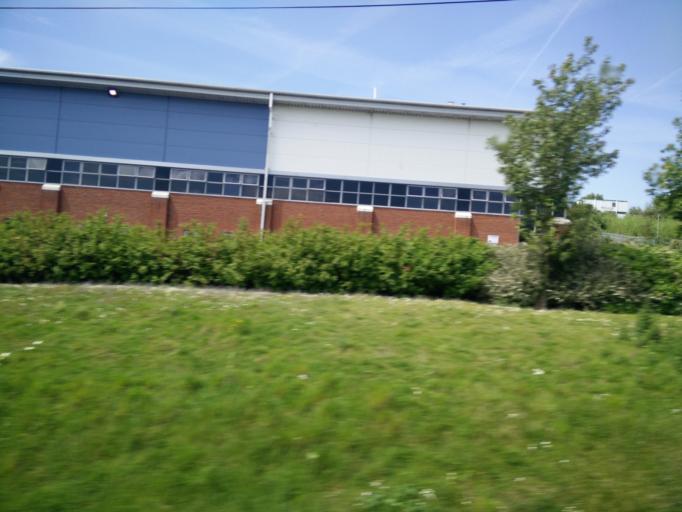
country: GB
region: England
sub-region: Luton
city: Luton
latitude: 51.8755
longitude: -0.3839
